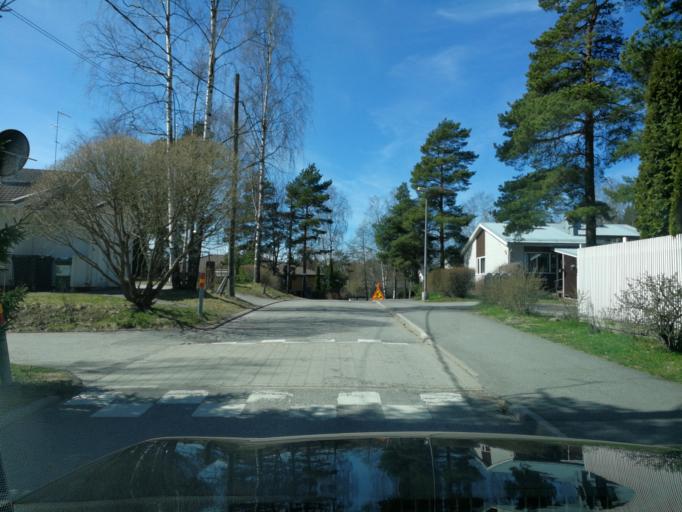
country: FI
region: Uusimaa
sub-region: Helsinki
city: Koukkuniemi
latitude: 60.1714
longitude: 24.7399
